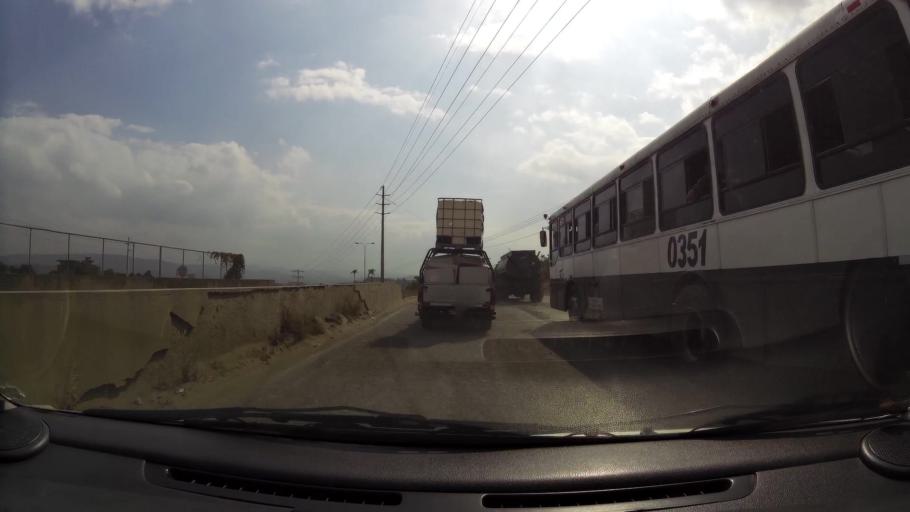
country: EC
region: Guayas
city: Santa Lucia
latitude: -2.1204
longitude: -79.9748
